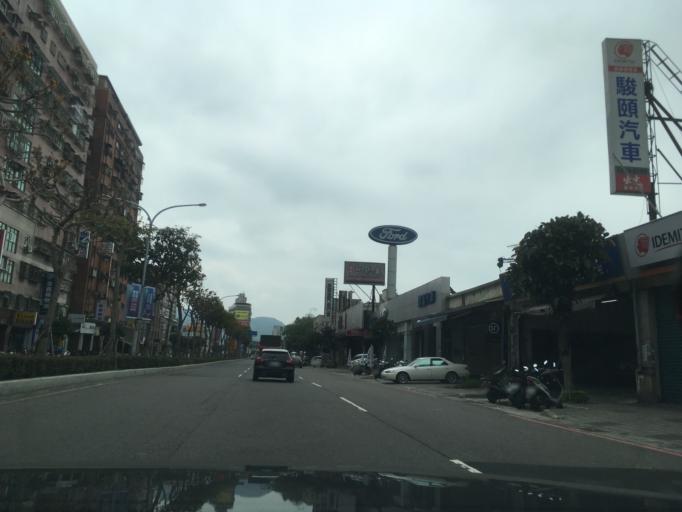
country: TW
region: Taipei
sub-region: Taipei
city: Banqiao
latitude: 24.9815
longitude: 121.4408
